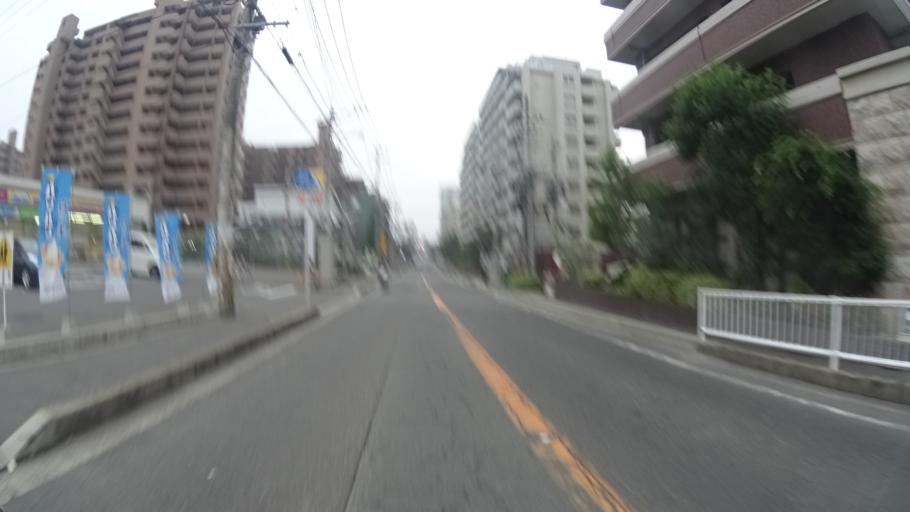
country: JP
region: Fukuoka
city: Onojo
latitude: 33.5434
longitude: 130.4573
